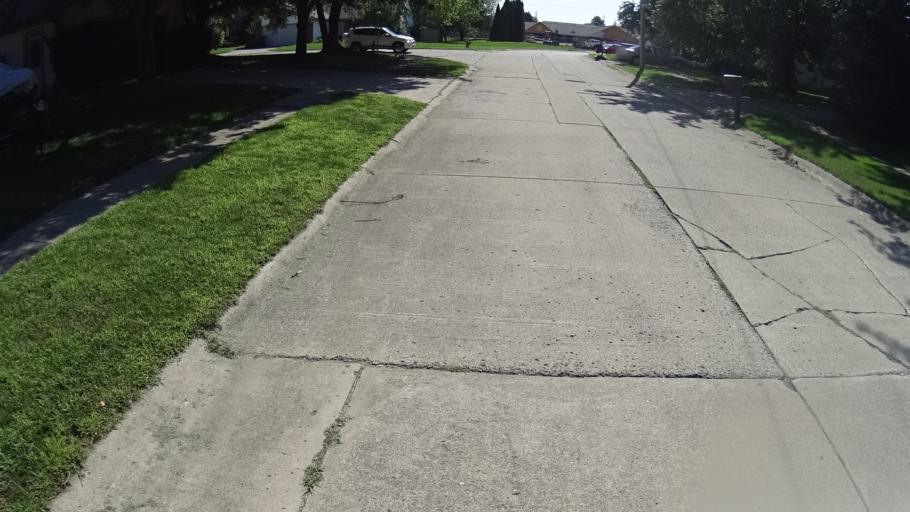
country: US
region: Indiana
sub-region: Madison County
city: Pendleton
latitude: 40.0051
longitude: -85.7350
